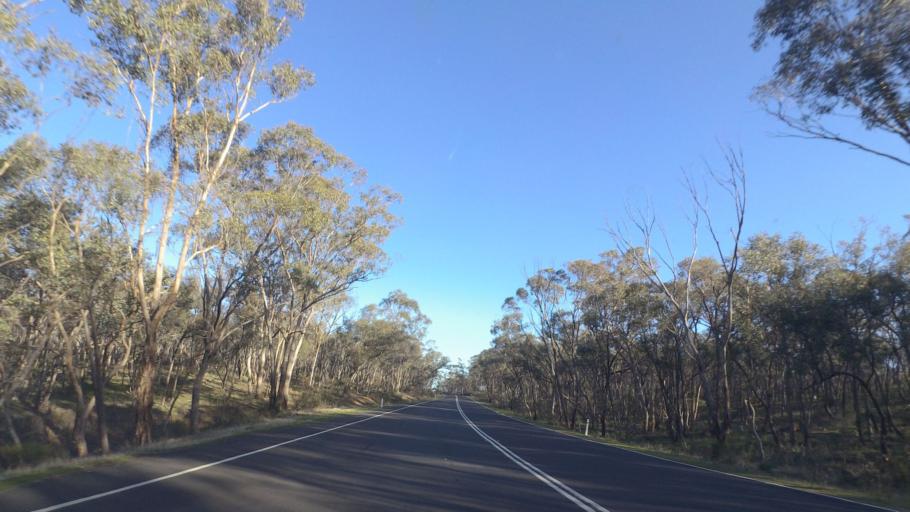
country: AU
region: Victoria
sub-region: Greater Bendigo
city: Kennington
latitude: -36.9111
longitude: 144.4930
